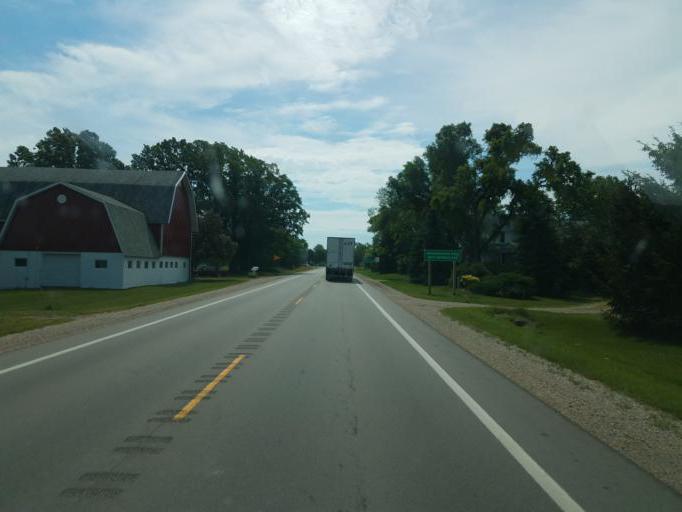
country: US
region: Michigan
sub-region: Eaton County
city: Charlotte
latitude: 42.6278
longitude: -84.8669
